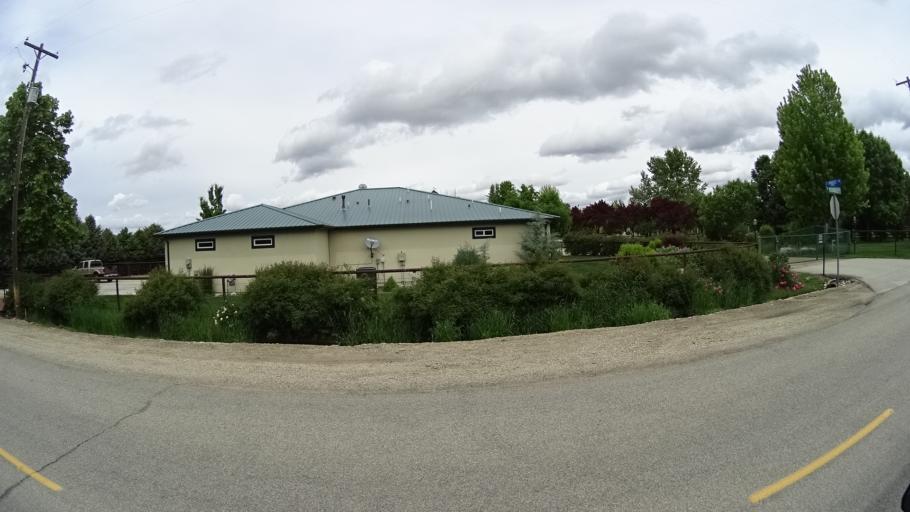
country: US
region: Idaho
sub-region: Ada County
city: Star
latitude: 43.6891
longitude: -116.4405
